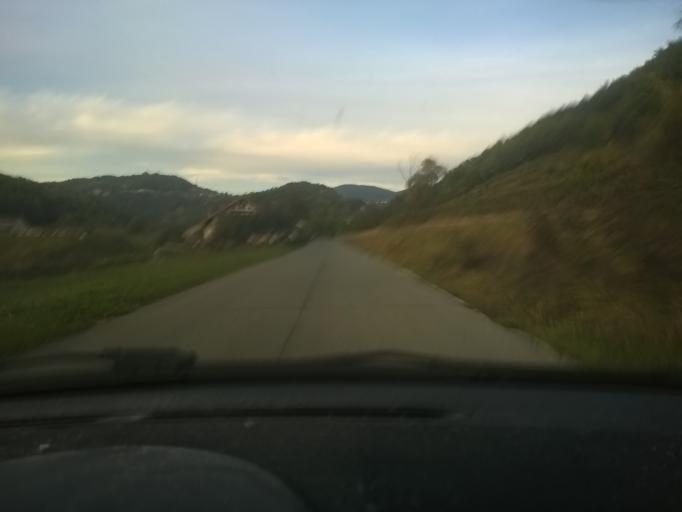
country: HR
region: Krapinsko-Zagorska
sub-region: Grad Krapina
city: Krapina
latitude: 46.1500
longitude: 15.8524
